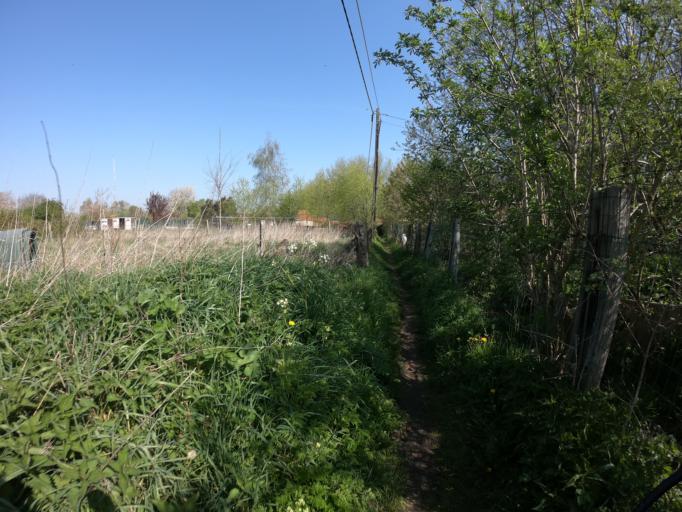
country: BE
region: Wallonia
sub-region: Province du Hainaut
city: Lessines
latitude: 50.7359
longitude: 3.8580
